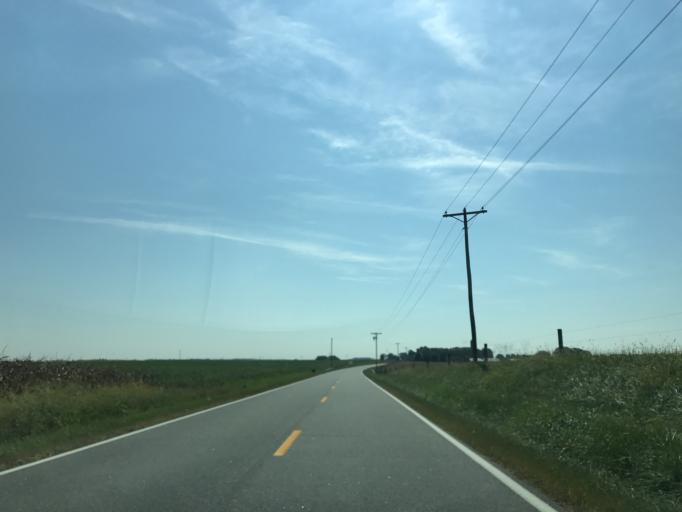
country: US
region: Maryland
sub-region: Queen Anne's County
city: Kingstown
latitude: 39.3174
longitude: -75.9404
